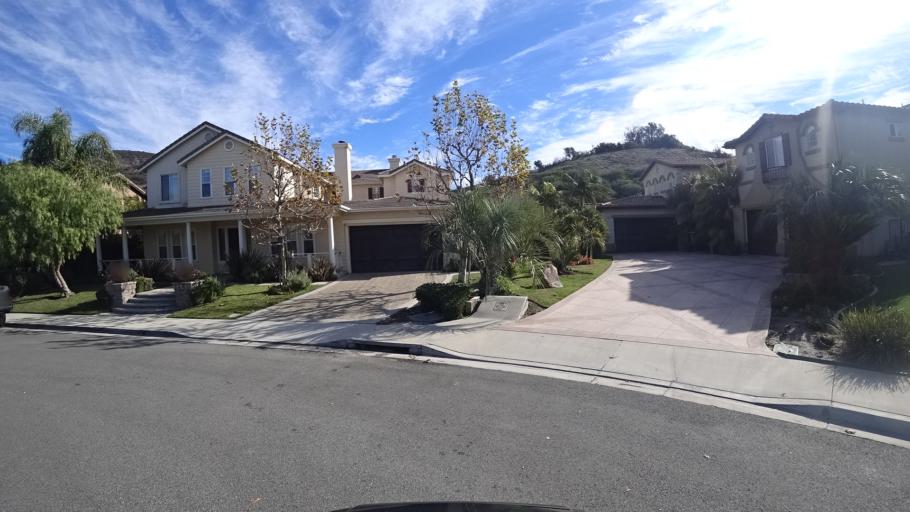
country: US
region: California
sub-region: Orange County
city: Portola Hills
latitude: 33.6902
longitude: -117.6192
